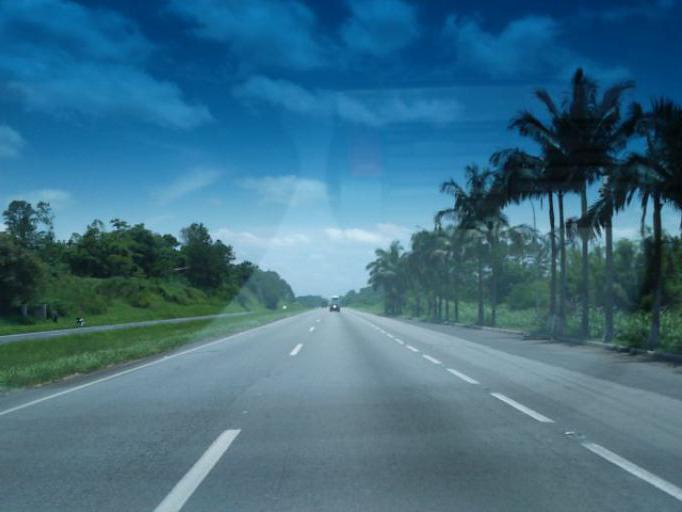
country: BR
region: Sao Paulo
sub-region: Registro
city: Registro
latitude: -24.4251
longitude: -47.7809
